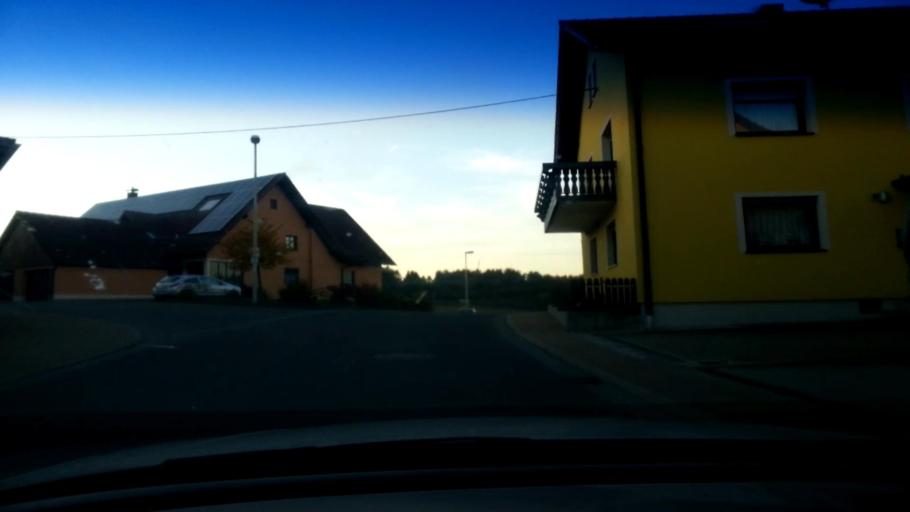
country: DE
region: Bavaria
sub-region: Upper Franconia
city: Heiligenstadt
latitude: 49.8464
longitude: 11.1184
